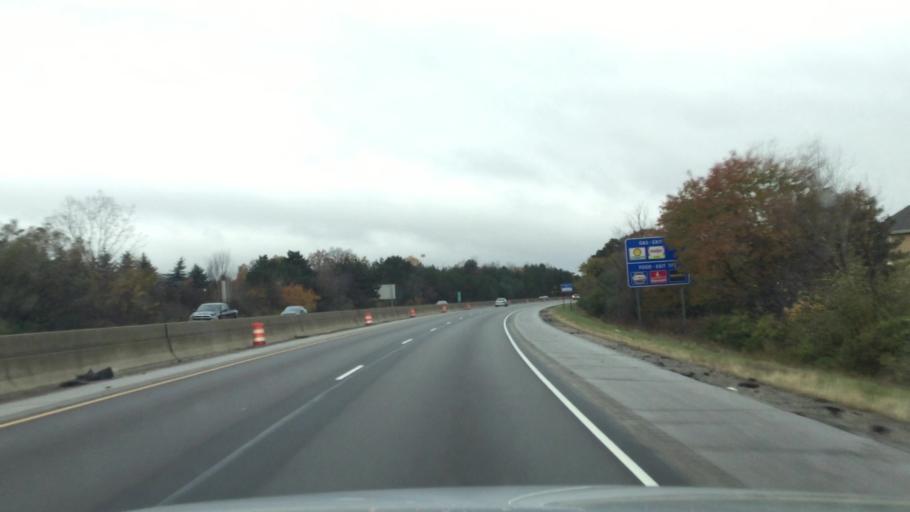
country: US
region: Michigan
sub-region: Washtenaw County
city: Ann Arbor
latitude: 42.2383
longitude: -83.7528
